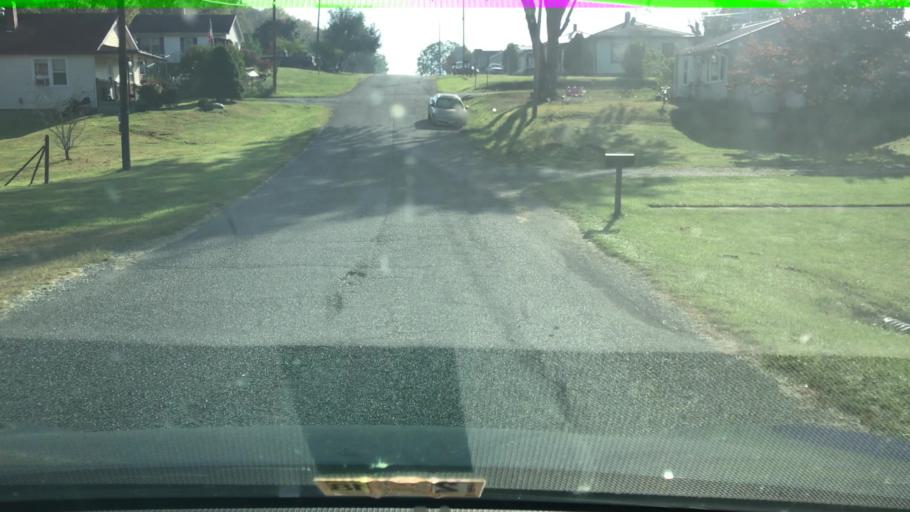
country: US
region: Virginia
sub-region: Pulaski County
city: Pulaski
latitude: 37.0498
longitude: -80.7638
